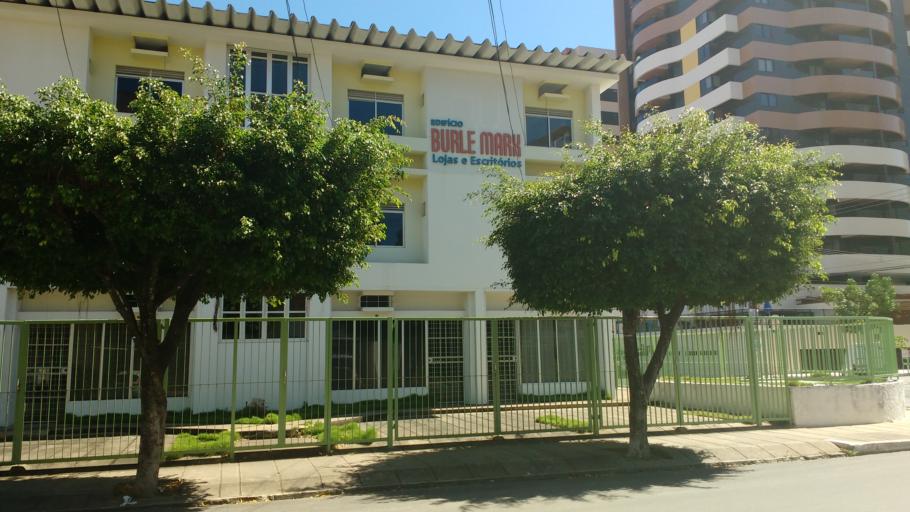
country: BR
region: Alagoas
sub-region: Maceio
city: Maceio
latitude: -9.6591
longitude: -35.7075
